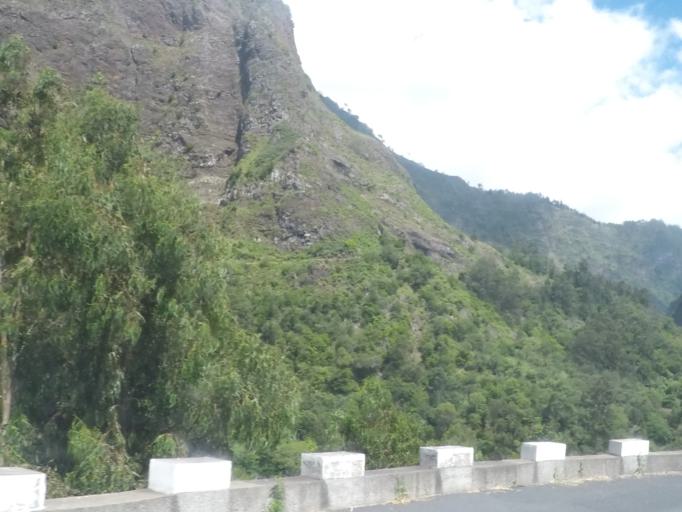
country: PT
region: Madeira
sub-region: Camara de Lobos
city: Curral das Freiras
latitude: 32.7080
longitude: -16.9722
